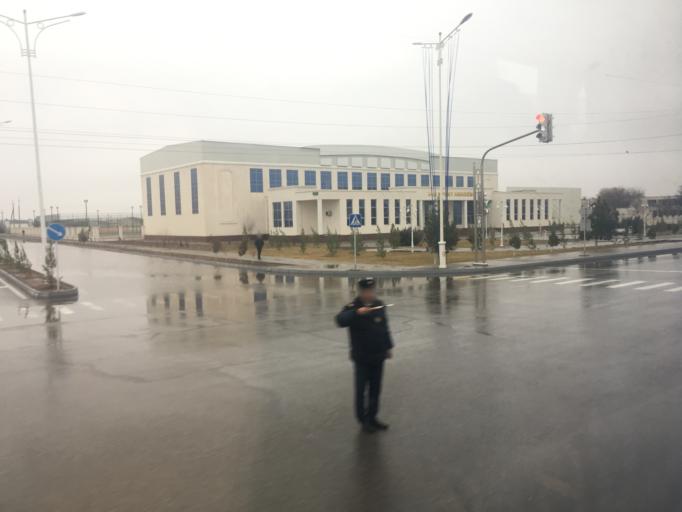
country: TM
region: Lebap
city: Turkmenabat
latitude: 39.0418
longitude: 63.5885
